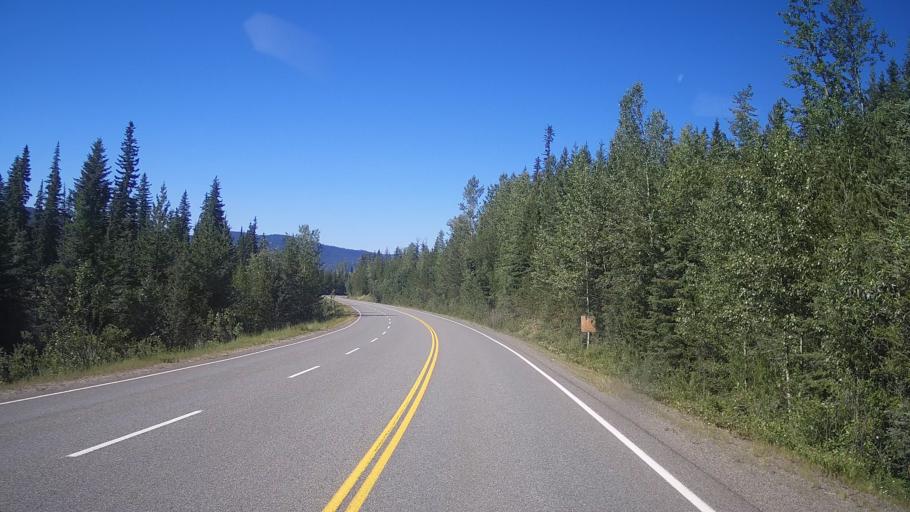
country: CA
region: British Columbia
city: Kamloops
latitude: 51.4897
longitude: -120.4598
